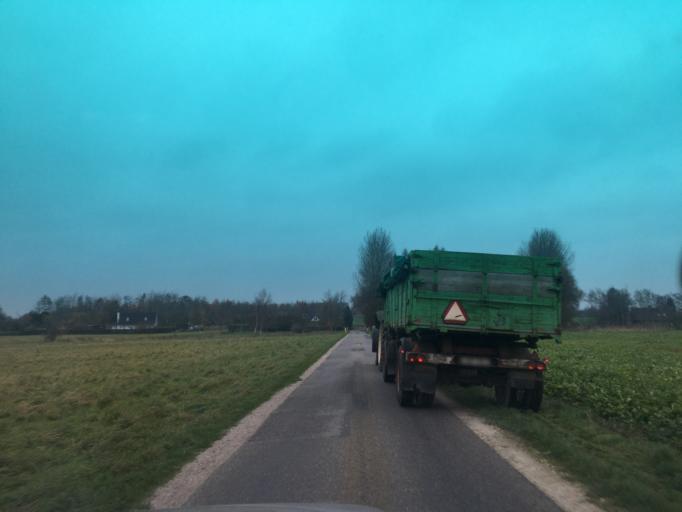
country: DK
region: Zealand
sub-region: Slagelse Kommune
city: Skaelskor
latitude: 55.2679
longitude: 11.4197
